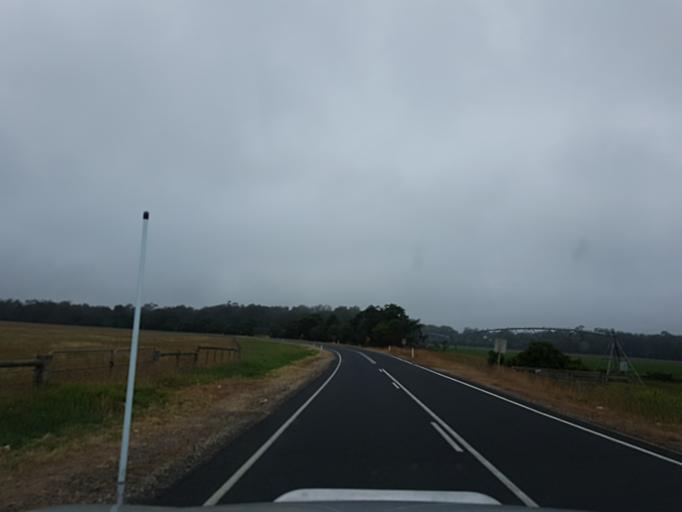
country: AU
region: Victoria
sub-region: Wellington
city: Sale
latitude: -38.0862
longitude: 147.0063
